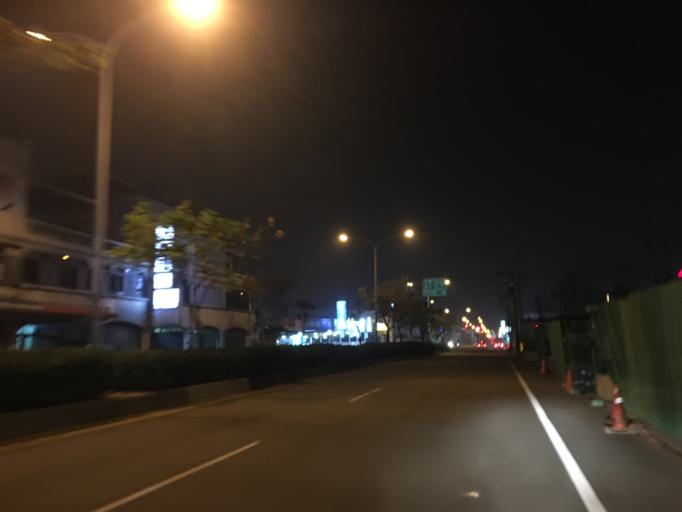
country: TW
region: Taiwan
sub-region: Hsinchu
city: Hsinchu
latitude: 24.6924
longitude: 120.8855
